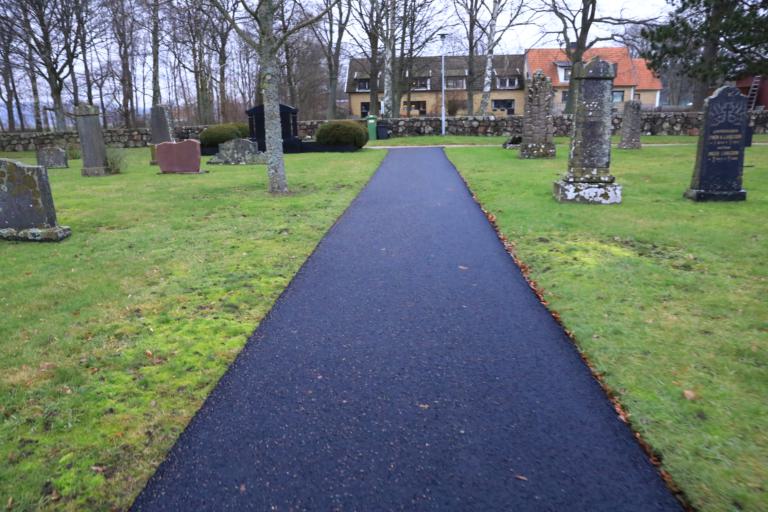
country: SE
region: Halland
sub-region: Varbergs Kommun
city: Tvaaker
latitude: 57.0470
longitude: 12.4000
